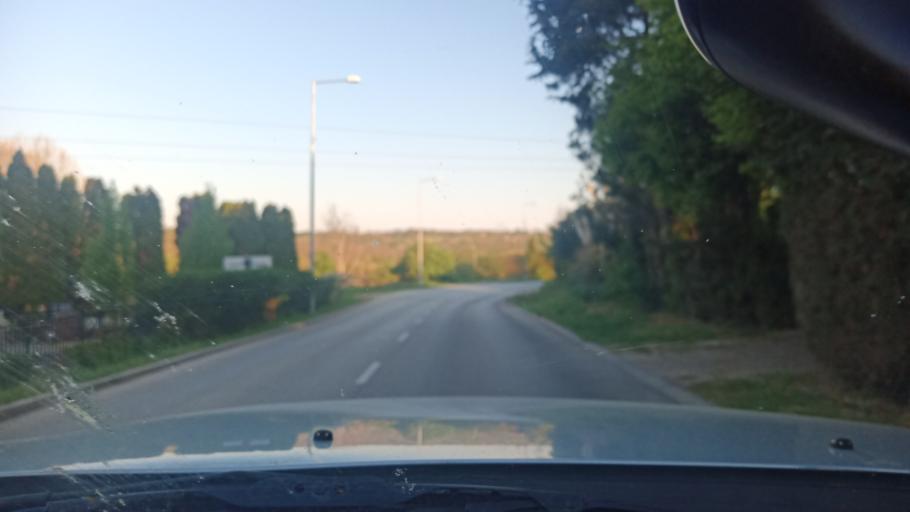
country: HU
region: Zala
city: Heviz
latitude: 46.7912
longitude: 17.1768
